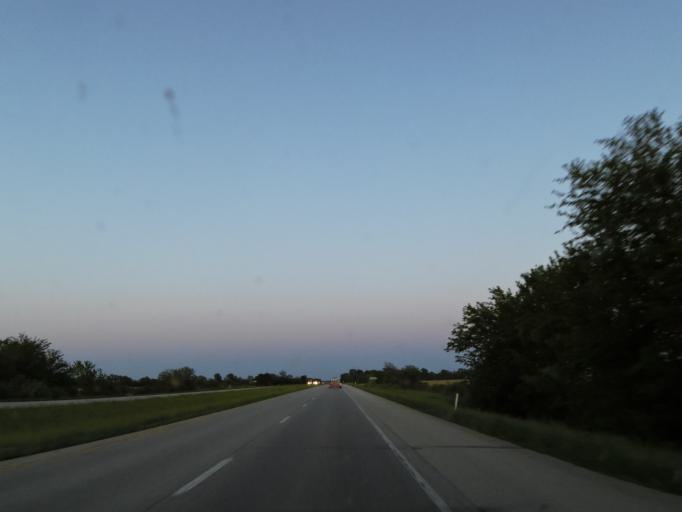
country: US
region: Indiana
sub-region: Boone County
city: Thorntown
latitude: 39.9869
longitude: -86.6981
